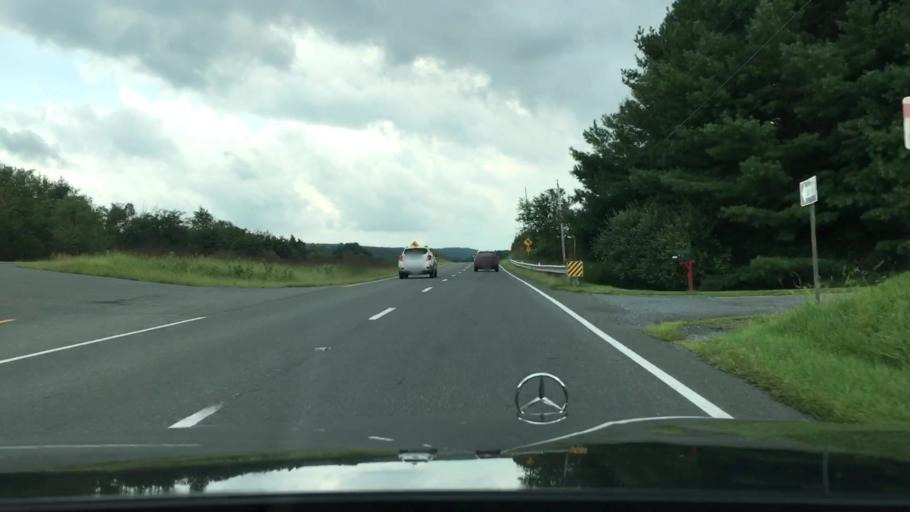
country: US
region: West Virginia
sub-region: Morgan County
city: Berkeley Springs
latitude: 39.4270
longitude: -78.3130
